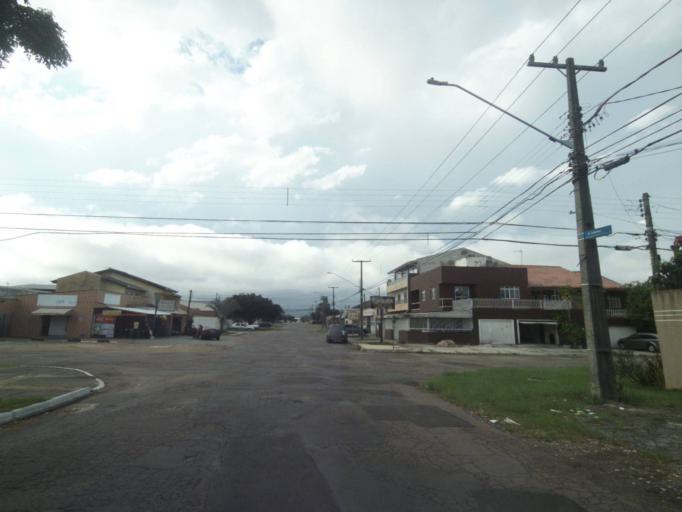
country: BR
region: Parana
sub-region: Pinhais
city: Pinhais
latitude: -25.4493
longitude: -49.2084
